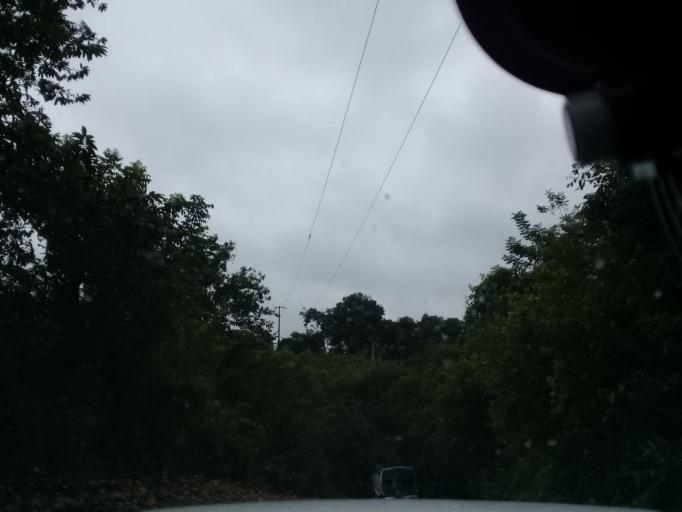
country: MX
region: Veracruz
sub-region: Chalma
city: San Pedro Coyutla
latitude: 21.2329
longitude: -98.4207
